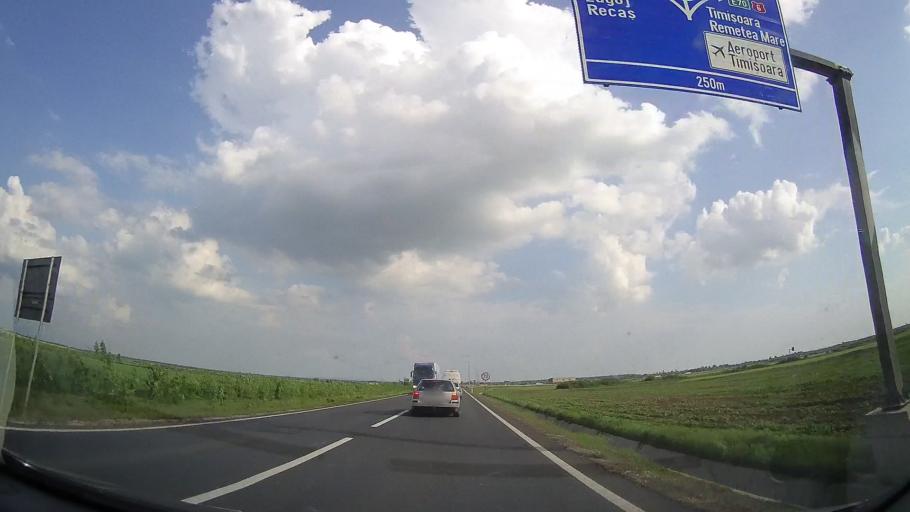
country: RO
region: Timis
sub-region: Comuna Remetea Mare
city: Remetea Mare
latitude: 45.7975
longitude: 21.4136
